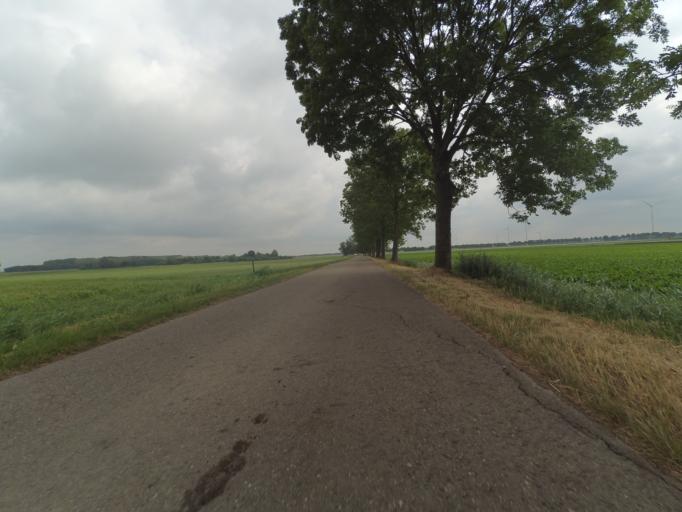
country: NL
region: North Brabant
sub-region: Gemeente Rucphen
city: Rucphen
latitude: 51.6017
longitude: 4.5721
